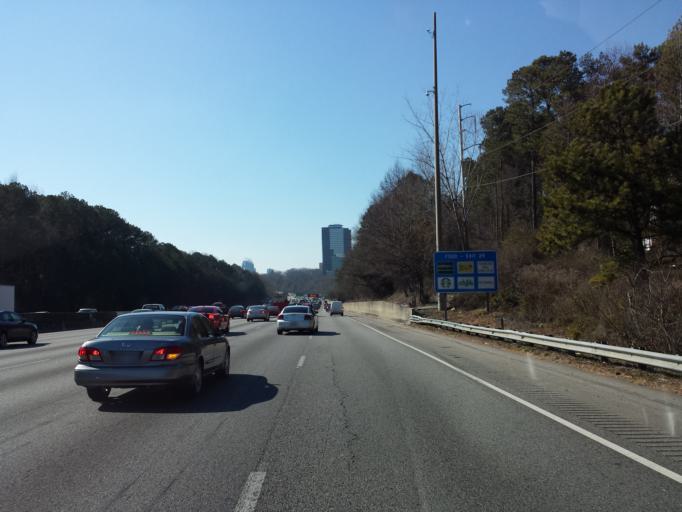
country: US
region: Georgia
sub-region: DeKalb County
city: Dunwoody
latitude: 33.9205
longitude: -84.3205
